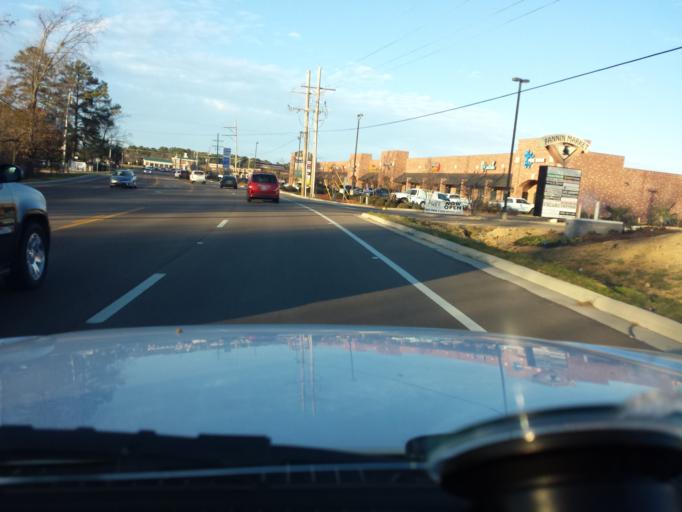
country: US
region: Mississippi
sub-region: Madison County
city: Ridgeland
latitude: 32.3791
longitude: -90.0428
